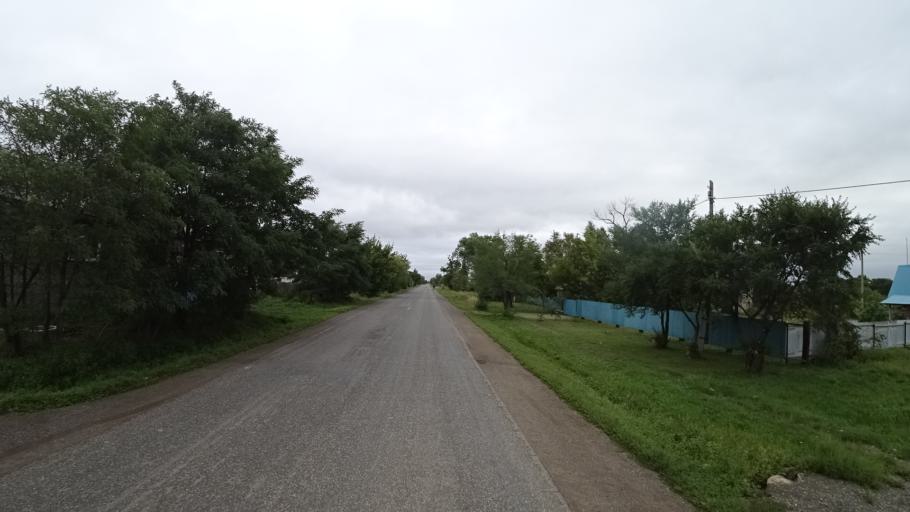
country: RU
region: Primorskiy
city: Chernigovka
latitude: 44.3277
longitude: 132.6022
